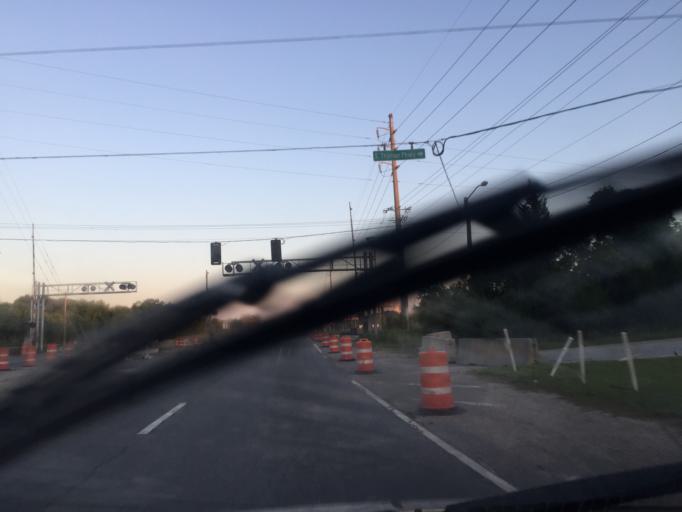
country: US
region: Georgia
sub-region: Chatham County
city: Savannah
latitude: 32.0735
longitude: -81.0746
